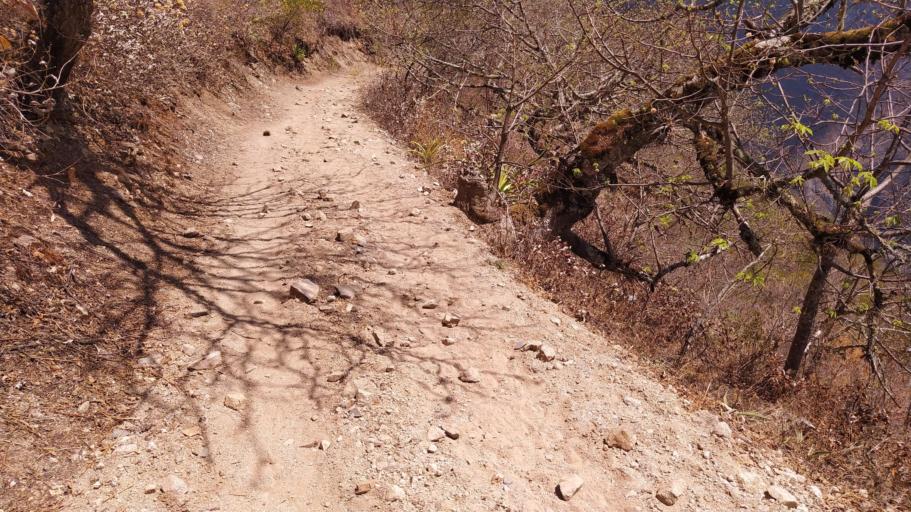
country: PE
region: Apurimac
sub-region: Provincia de Abancay
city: Cachora
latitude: -13.4334
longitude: -72.8244
